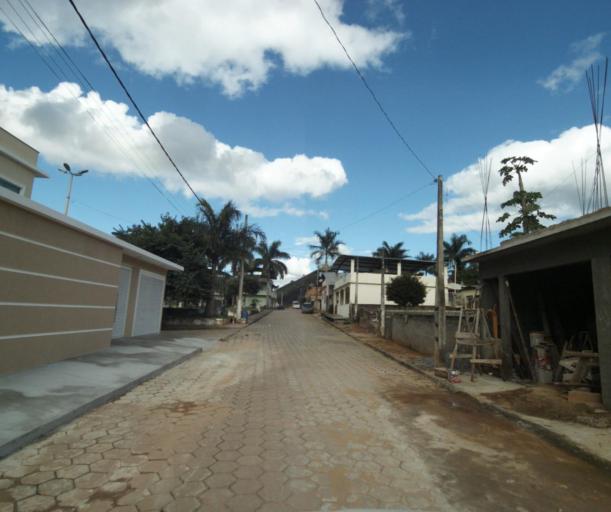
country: BR
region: Espirito Santo
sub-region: Irupi
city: Irupi
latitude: -20.5380
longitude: -41.6585
